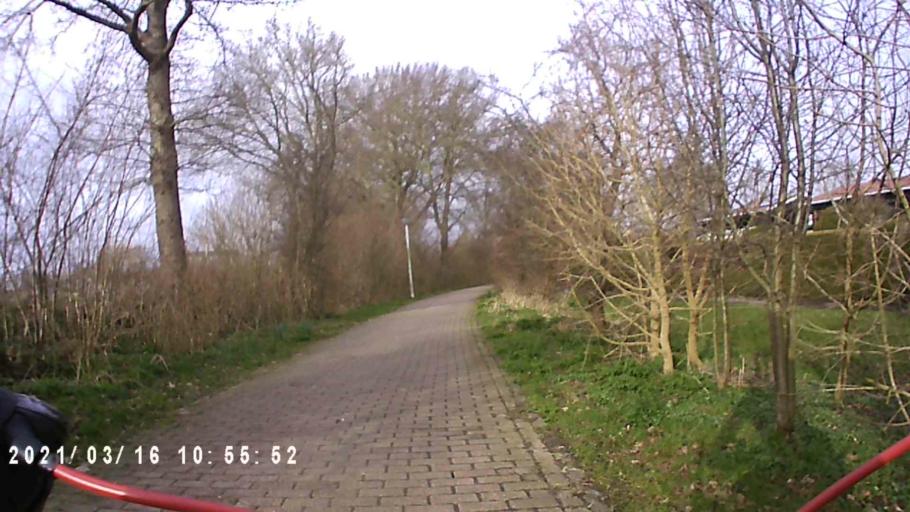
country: NL
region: Friesland
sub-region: Gemeente Dongeradeel
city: Dokkum
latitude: 53.3261
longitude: 6.0146
